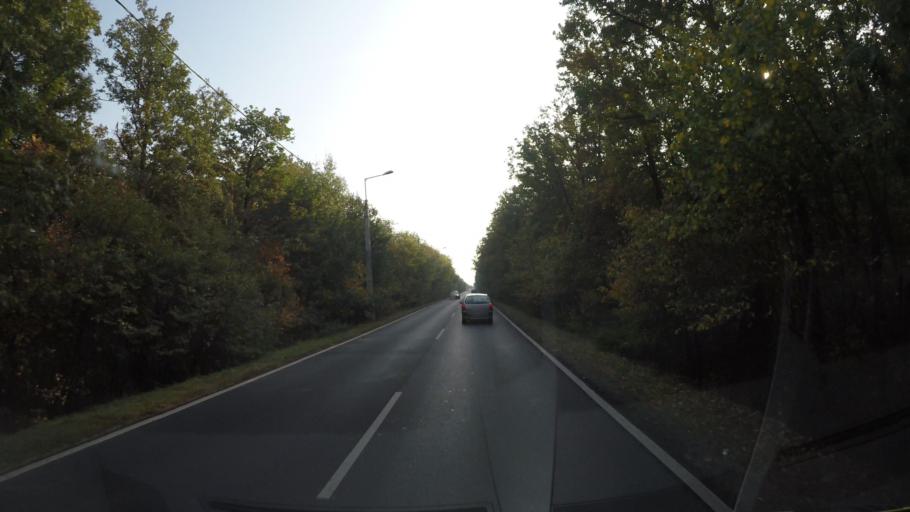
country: HU
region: Budapest
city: Budapest XXII. keruelet
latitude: 47.4408
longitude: 19.0013
